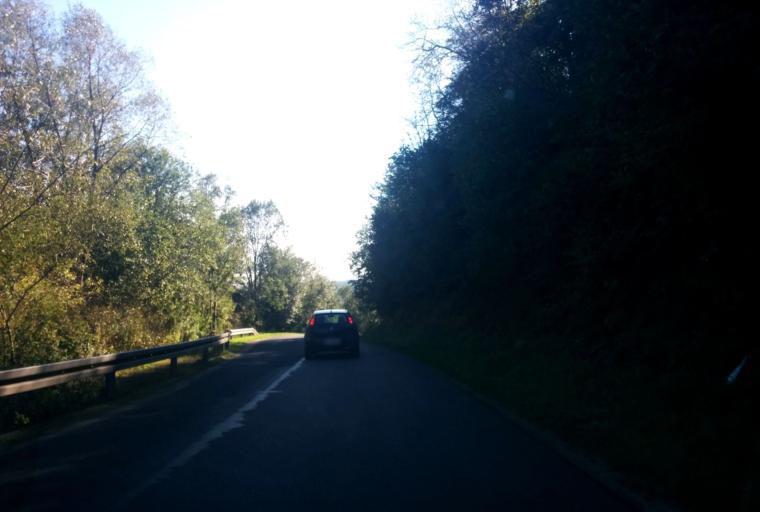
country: PL
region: Subcarpathian Voivodeship
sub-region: Powiat leski
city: Polanczyk
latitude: 49.3276
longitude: 22.4176
